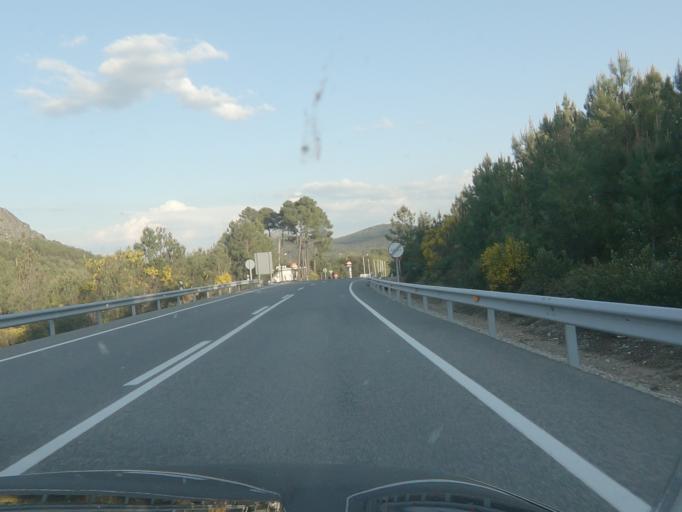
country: PT
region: Portalegre
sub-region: Portalegre
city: Sao Juliao
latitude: 39.3476
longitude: -7.3003
